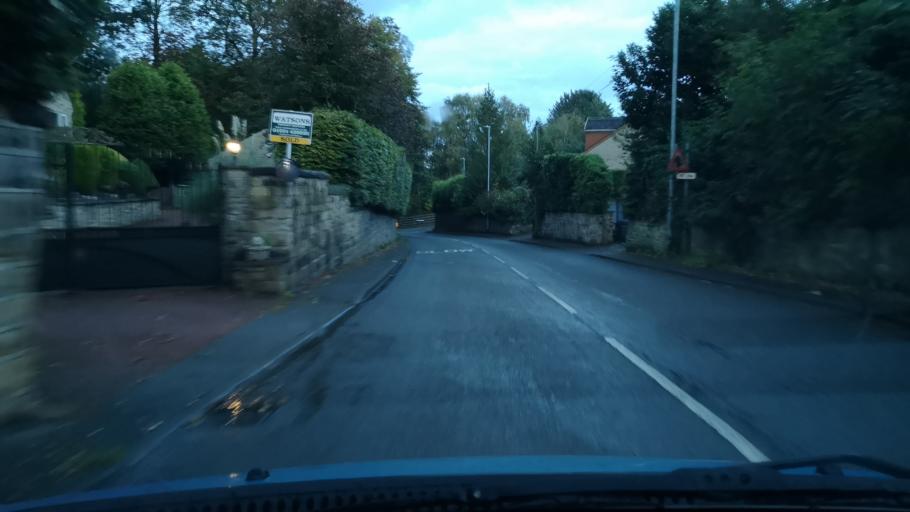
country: GB
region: England
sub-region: Kirklees
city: Batley
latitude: 53.7227
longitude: -1.6317
